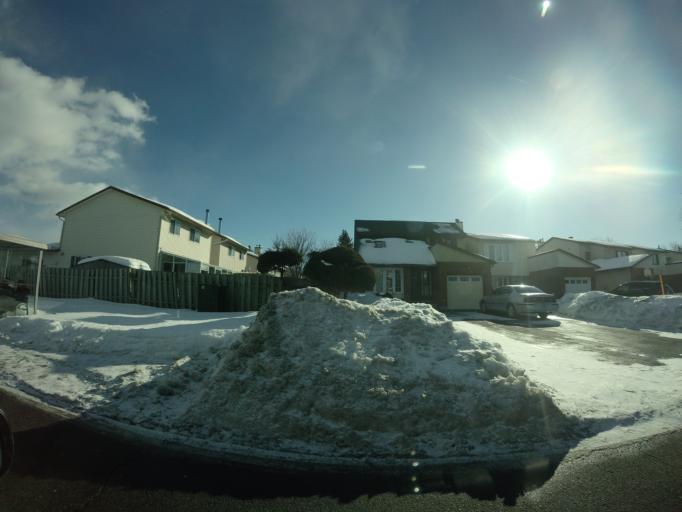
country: CA
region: Ontario
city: Ottawa
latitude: 45.4243
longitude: -75.6105
